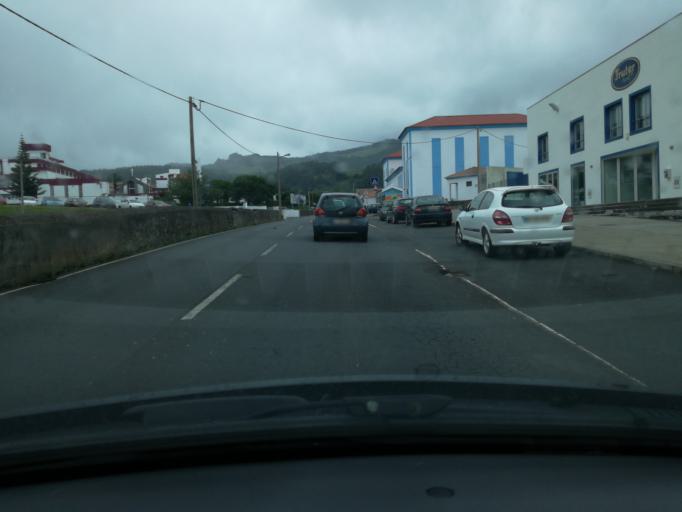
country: PT
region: Azores
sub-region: Angra do Heroismo
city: Angra do Heroismo
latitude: 38.6691
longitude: -27.2154
